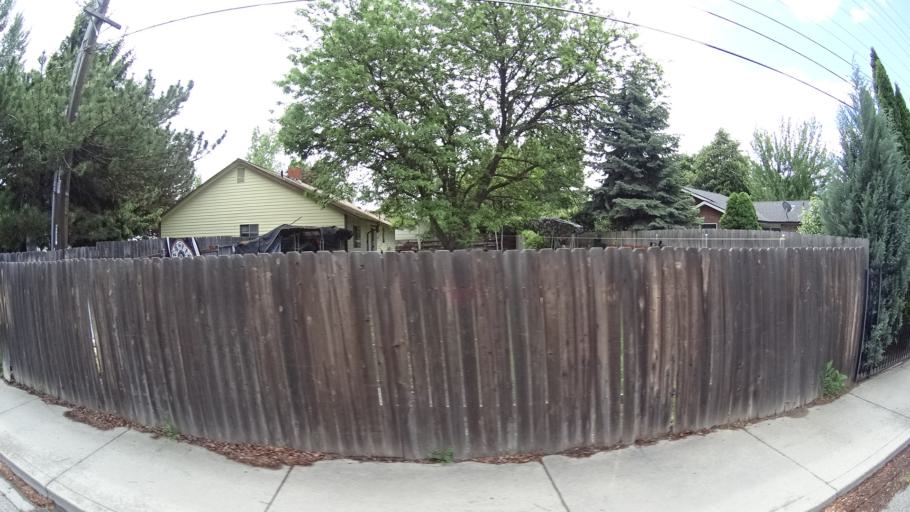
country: US
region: Idaho
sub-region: Ada County
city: Boise
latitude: 43.5697
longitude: -116.1734
